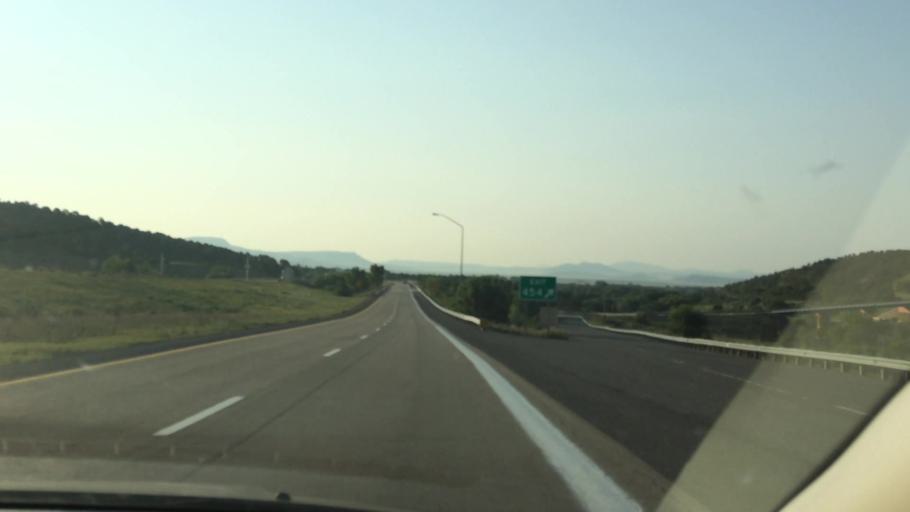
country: US
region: New Mexico
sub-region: Colfax County
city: Raton
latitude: 36.9196
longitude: -104.4490
